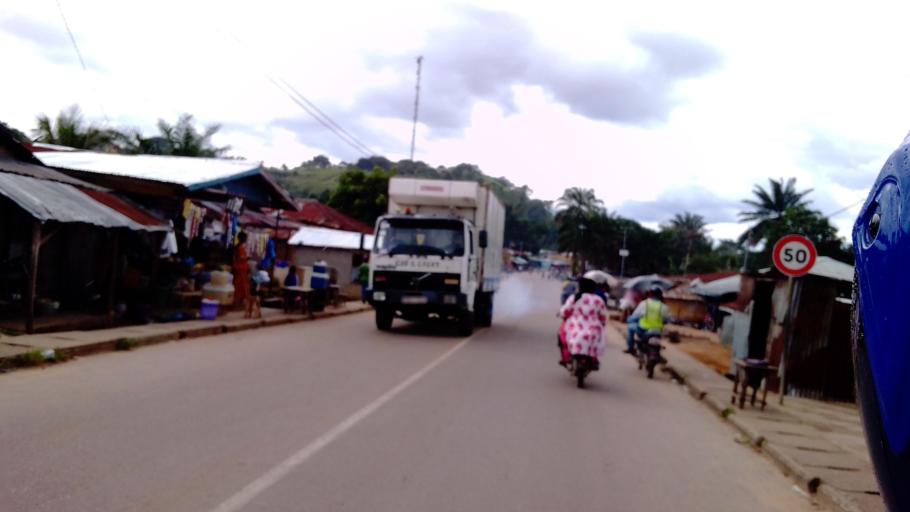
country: SL
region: Eastern Province
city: Koidu
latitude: 8.6476
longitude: -10.9747
